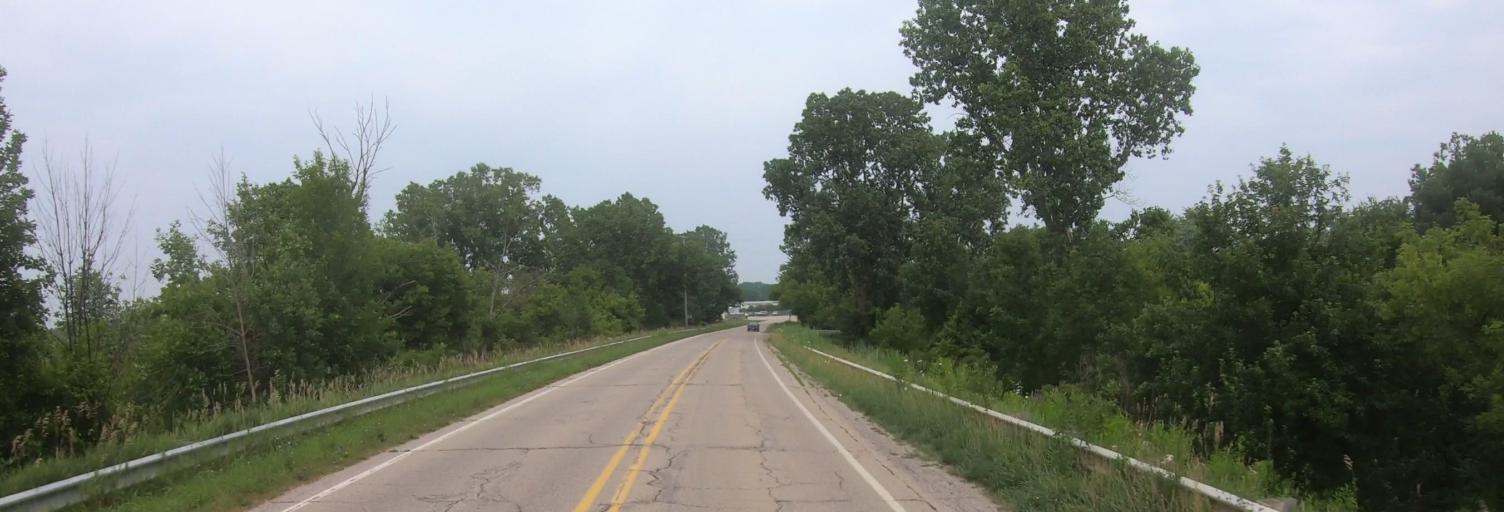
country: US
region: Michigan
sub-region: Shiawassee County
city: Durand
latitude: 42.9243
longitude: -84.0091
